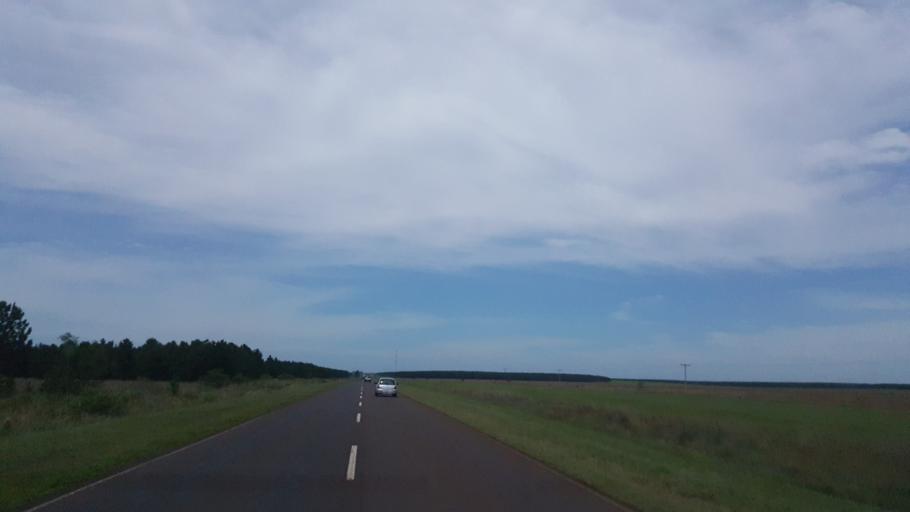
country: PY
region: Itapua
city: San Juan del Parana
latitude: -27.5103
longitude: -56.1350
